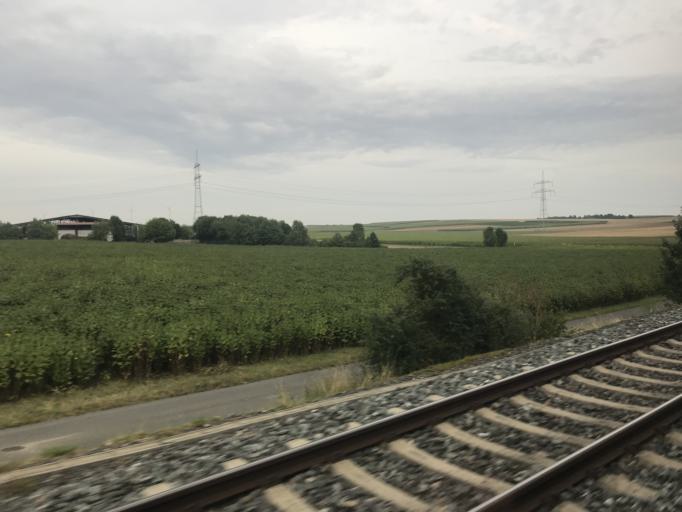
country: DE
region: Bavaria
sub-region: Regierungsbezirk Unterfranken
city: Oberpleichfeld
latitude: 49.8844
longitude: 10.0895
